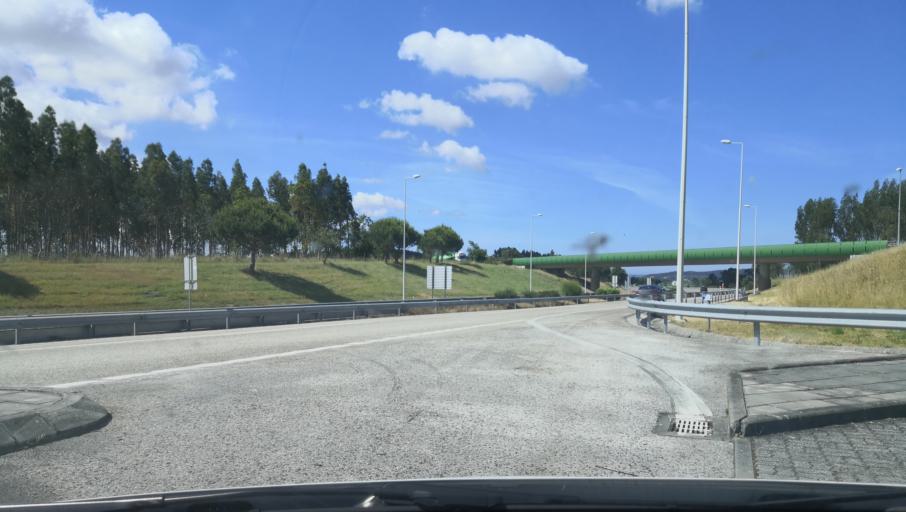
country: PT
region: Coimbra
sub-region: Montemor-O-Velho
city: Montemor-o-Velho
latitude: 40.1912
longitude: -8.6966
